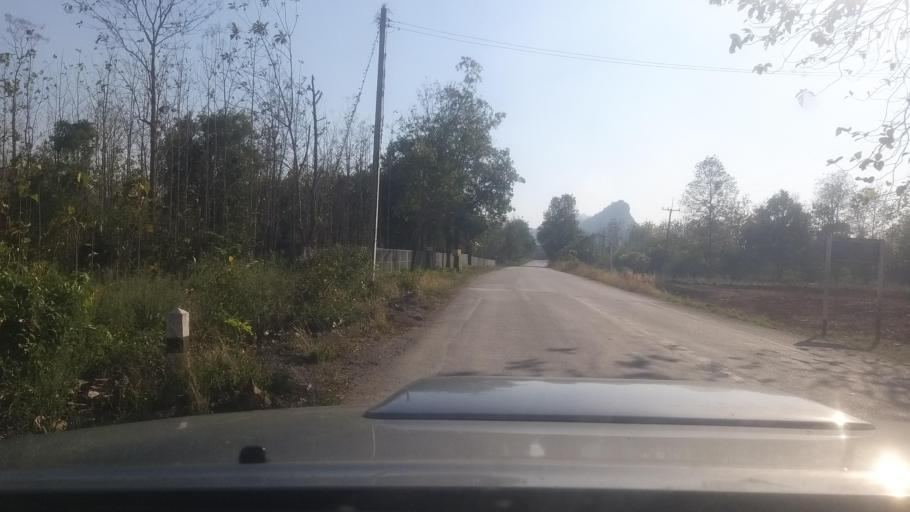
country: TH
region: Phrae
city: Phrae
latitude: 18.2509
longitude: 99.9923
